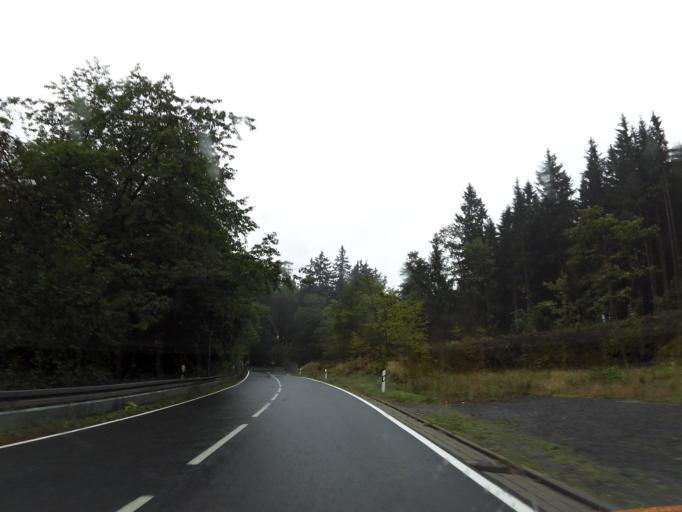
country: DE
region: Saxony-Anhalt
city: Hasselfelde
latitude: 51.6479
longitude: 10.9218
